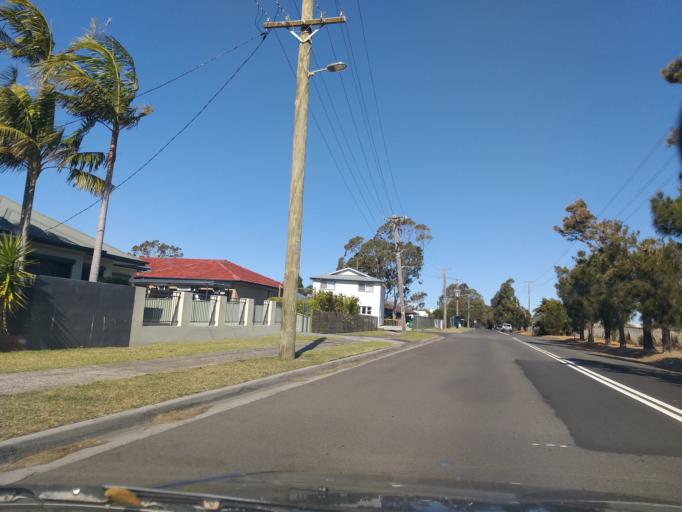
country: AU
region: New South Wales
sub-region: Wollongong
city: Bulli
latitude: -34.3530
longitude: 150.9142
